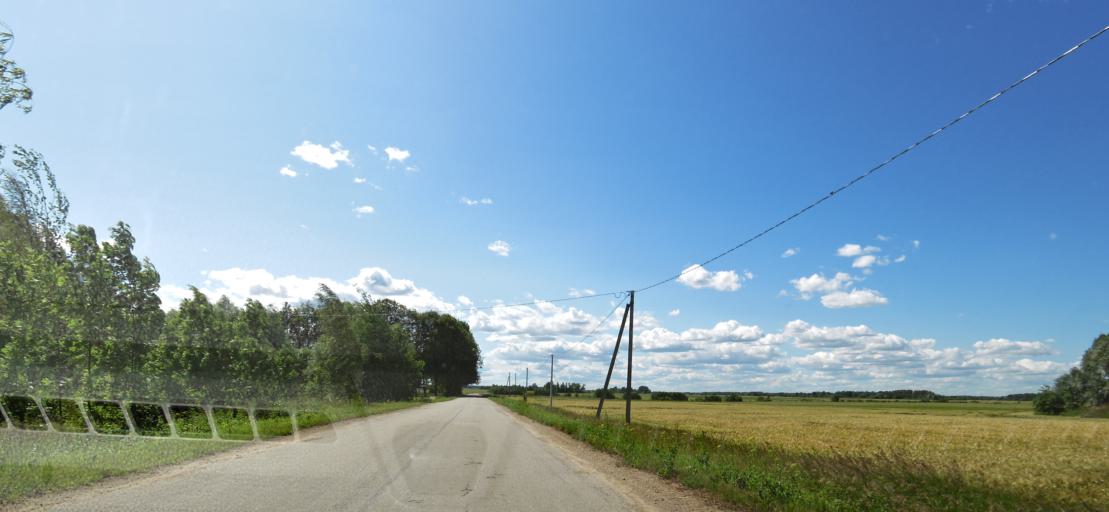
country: LV
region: Bauskas Rajons
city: Bauska
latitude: 56.2395
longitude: 24.2274
